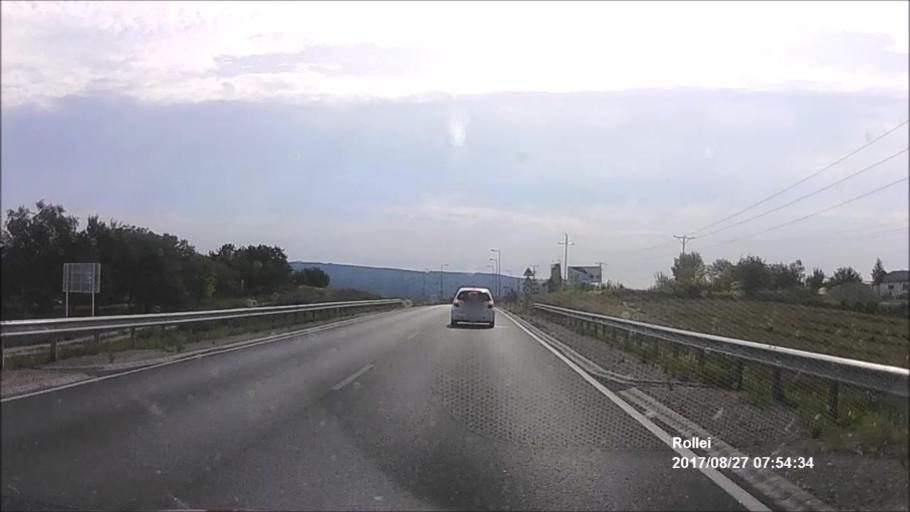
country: HU
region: Zala
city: Keszthely
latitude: 46.7823
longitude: 17.2492
